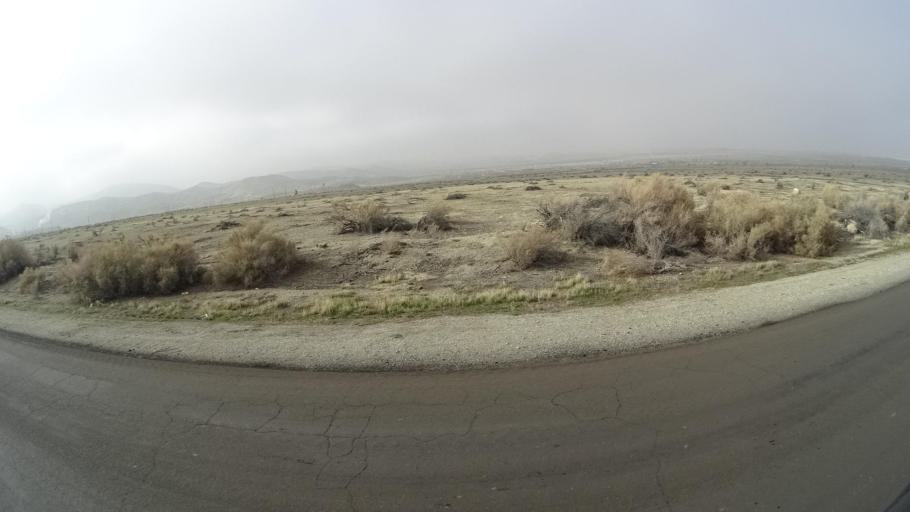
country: US
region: California
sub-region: Kern County
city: Maricopa
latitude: 35.0400
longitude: -119.3670
